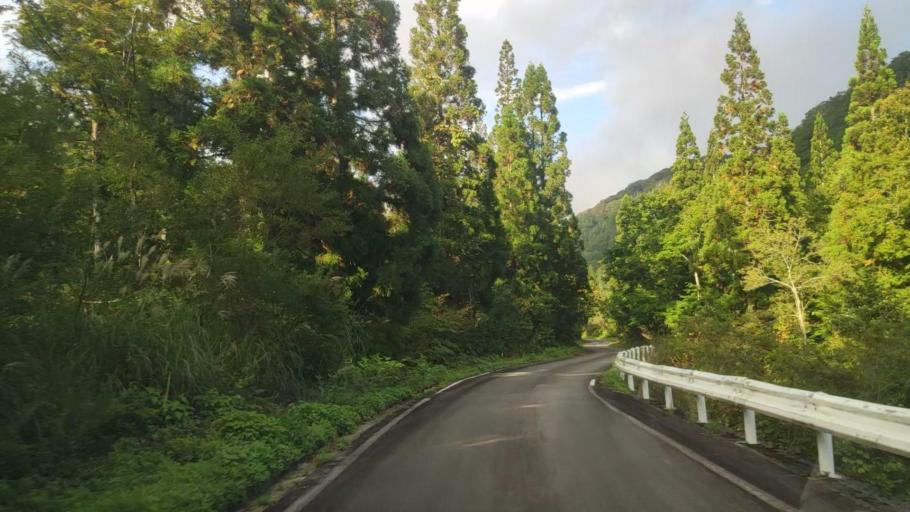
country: JP
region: Toyama
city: Yatsuomachi-higashikumisaka
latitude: 36.3692
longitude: 137.0763
